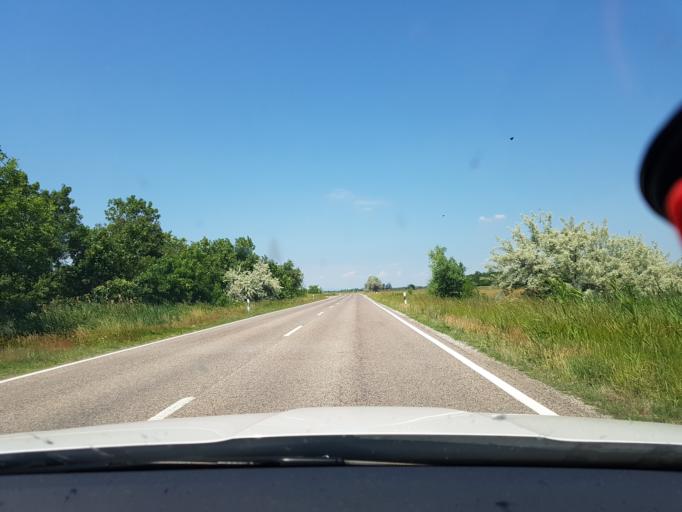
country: HU
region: Hajdu-Bihar
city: Egyek
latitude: 47.5676
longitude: 20.8611
